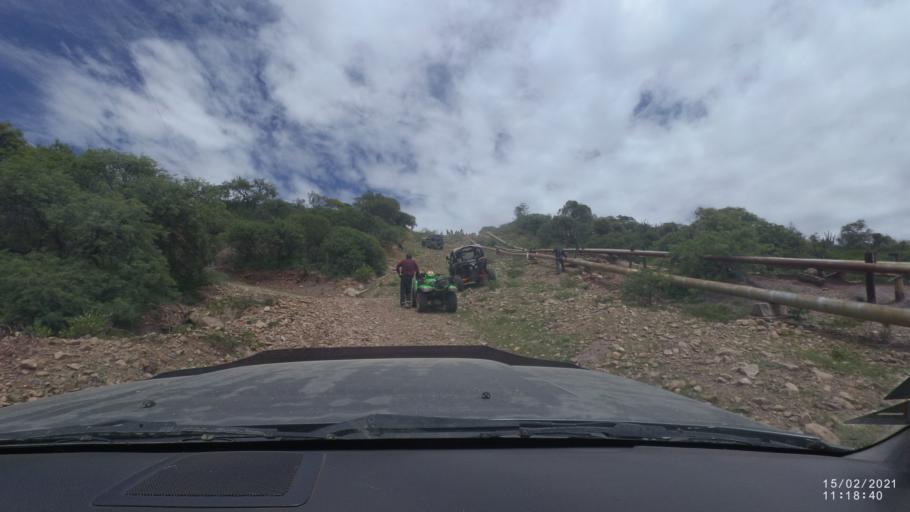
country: BO
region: Cochabamba
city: Sipe Sipe
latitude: -17.5497
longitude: -66.2993
